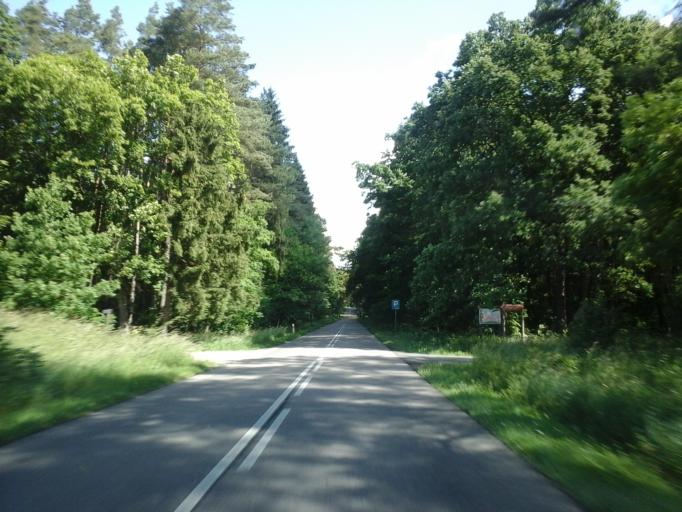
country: PL
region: West Pomeranian Voivodeship
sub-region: Powiat lobeski
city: Lobez
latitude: 53.5918
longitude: 15.5980
